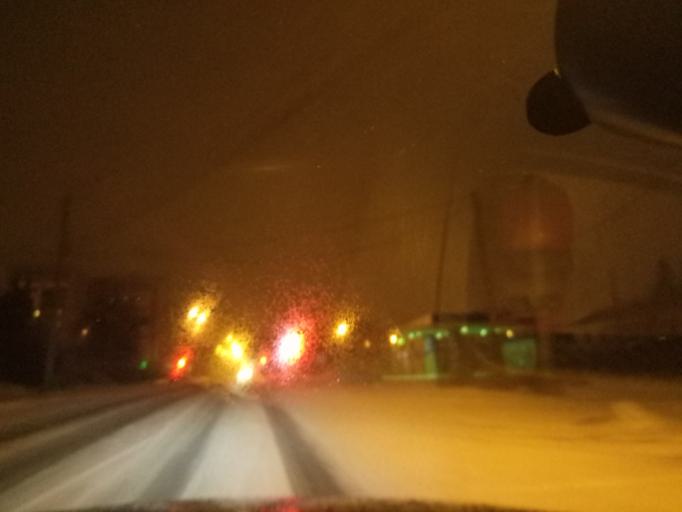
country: RU
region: Tula
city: Novomoskovsk
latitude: 54.0035
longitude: 38.2961
